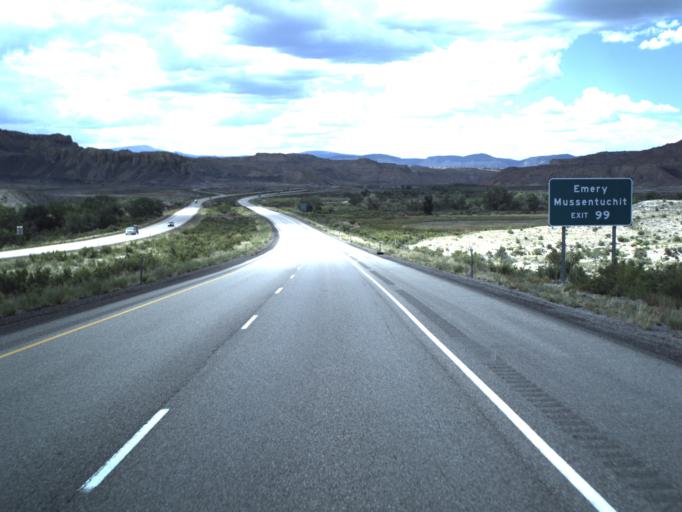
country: US
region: Utah
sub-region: Emery County
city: Ferron
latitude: 38.8154
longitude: -111.1929
